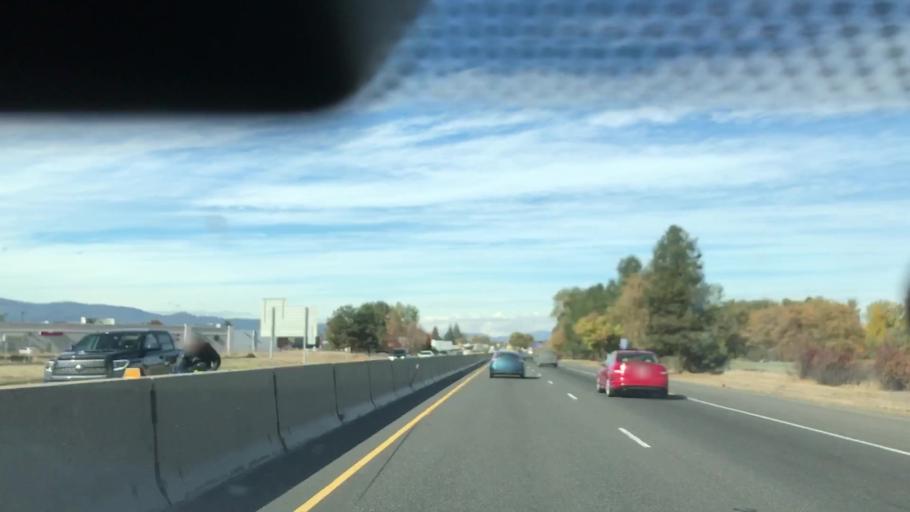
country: US
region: Oregon
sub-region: Jackson County
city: Medford
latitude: 42.3171
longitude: -122.8570
